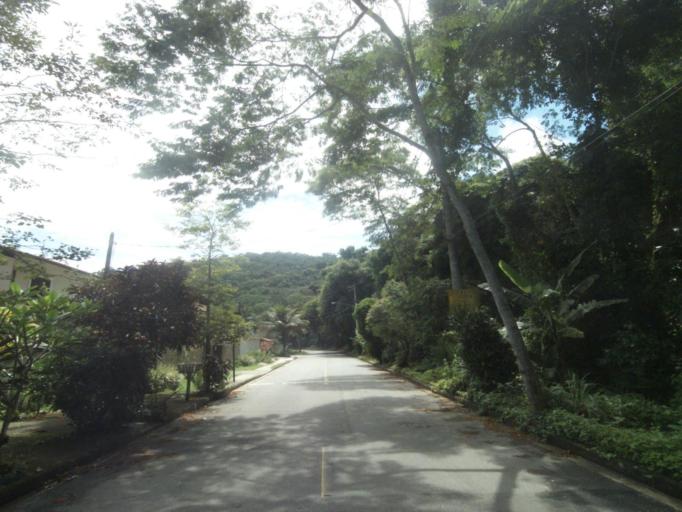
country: BR
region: Rio de Janeiro
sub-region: Niteroi
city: Niteroi
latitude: -22.9534
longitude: -43.0221
